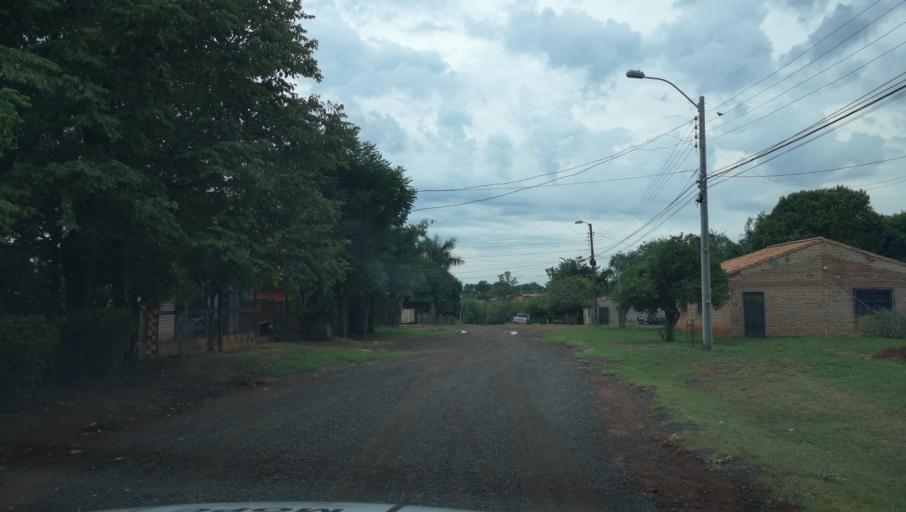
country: PY
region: Misiones
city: Santa Maria
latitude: -26.8903
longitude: -57.0406
